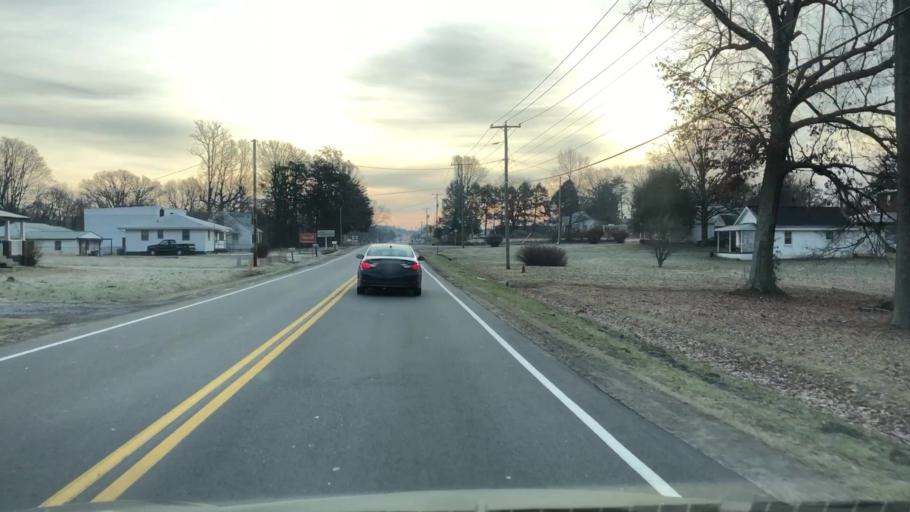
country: US
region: Virginia
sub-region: Campbell County
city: Timberlake
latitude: 37.3324
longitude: -79.2564
